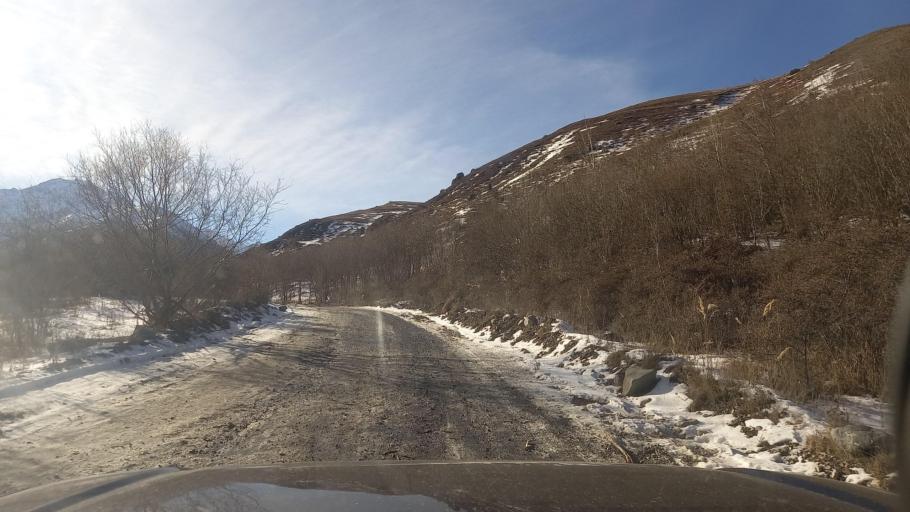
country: RU
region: Ingushetiya
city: Dzhayrakh
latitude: 42.8557
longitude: 44.5209
